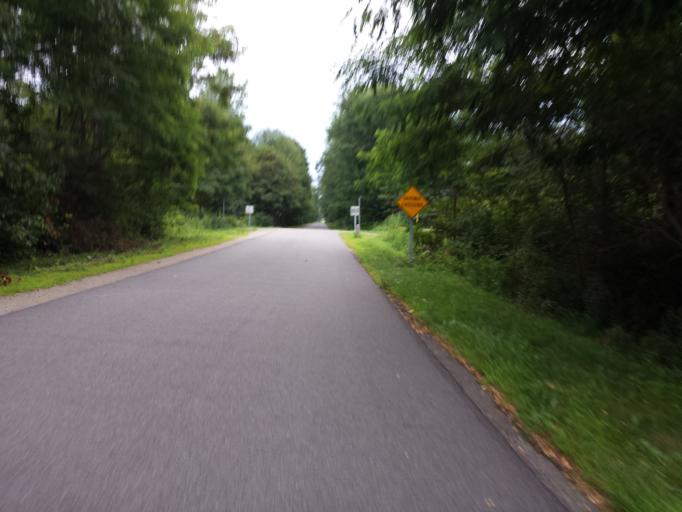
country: US
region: New York
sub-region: Dutchess County
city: Red Oaks Mill
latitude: 41.6503
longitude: -73.8578
